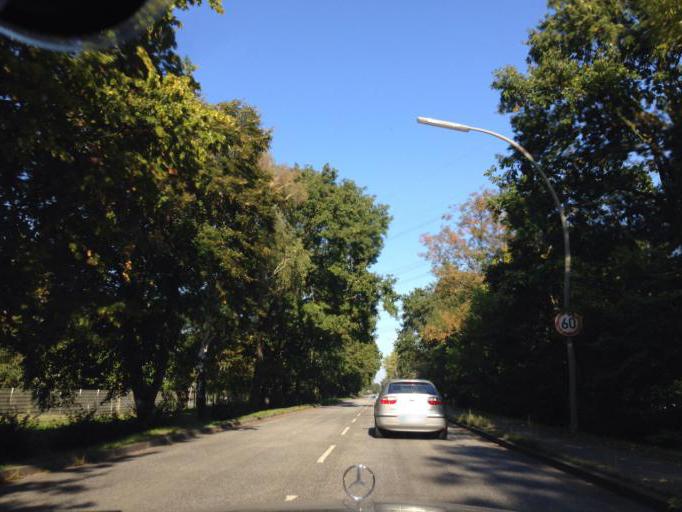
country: DE
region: Schleswig-Holstein
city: Stapelfeld
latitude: 53.6327
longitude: 10.1850
